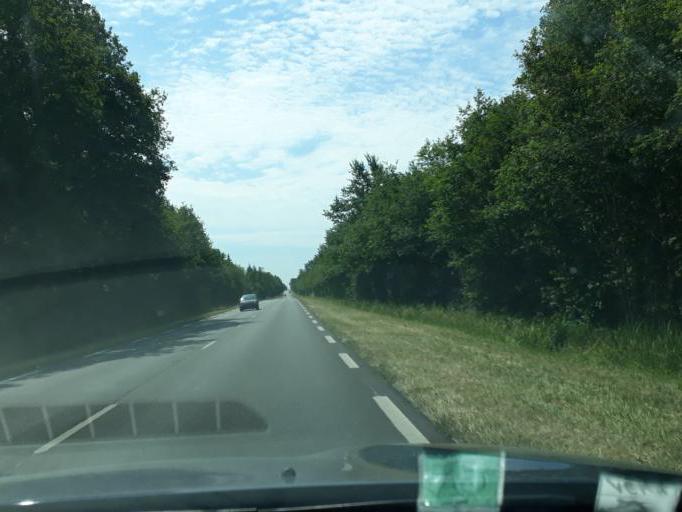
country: FR
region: Centre
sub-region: Departement du Loiret
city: Menestreau-en-Villette
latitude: 47.6617
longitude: 1.9799
